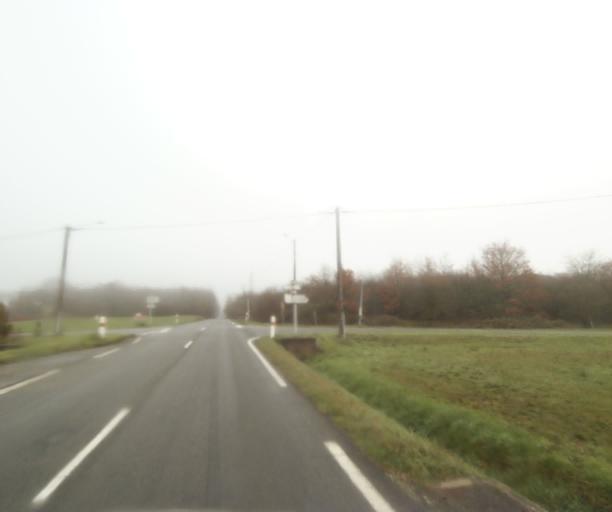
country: FR
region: Midi-Pyrenees
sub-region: Departement de la Haute-Garonne
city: Villaudric
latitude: 43.8473
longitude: 1.4616
